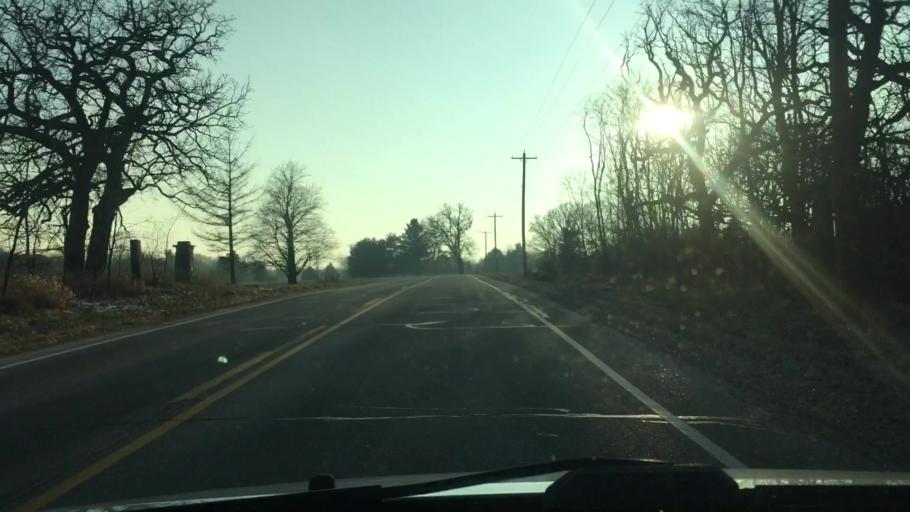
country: US
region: Wisconsin
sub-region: Waukesha County
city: Dousman
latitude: 42.9716
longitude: -88.4720
